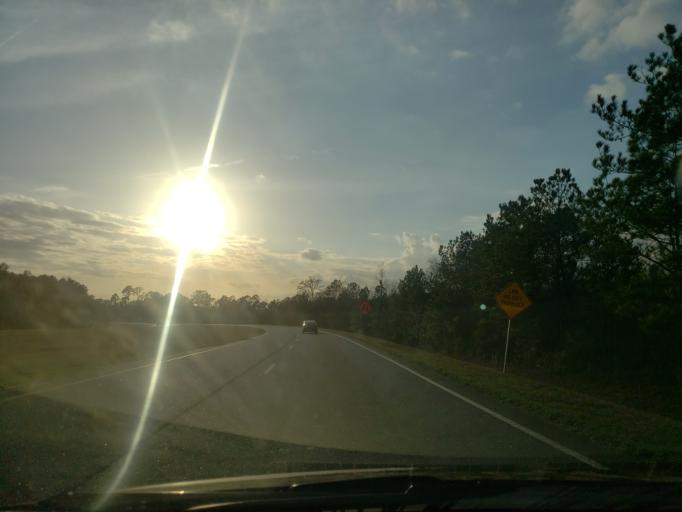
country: US
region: Georgia
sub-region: Chatham County
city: Bloomingdale
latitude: 32.1465
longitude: -81.3031
